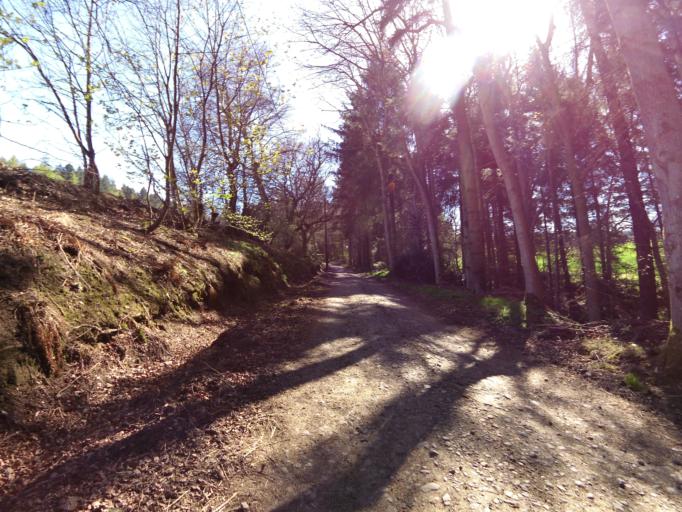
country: GB
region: Scotland
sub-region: Fife
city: Cupar
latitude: 56.3922
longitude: -3.0708
